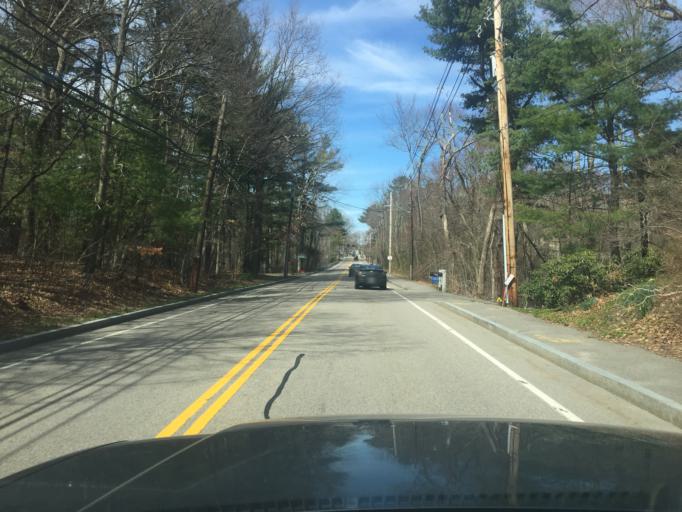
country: US
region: Massachusetts
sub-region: Norfolk County
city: Needham
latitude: 42.2653
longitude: -71.2376
